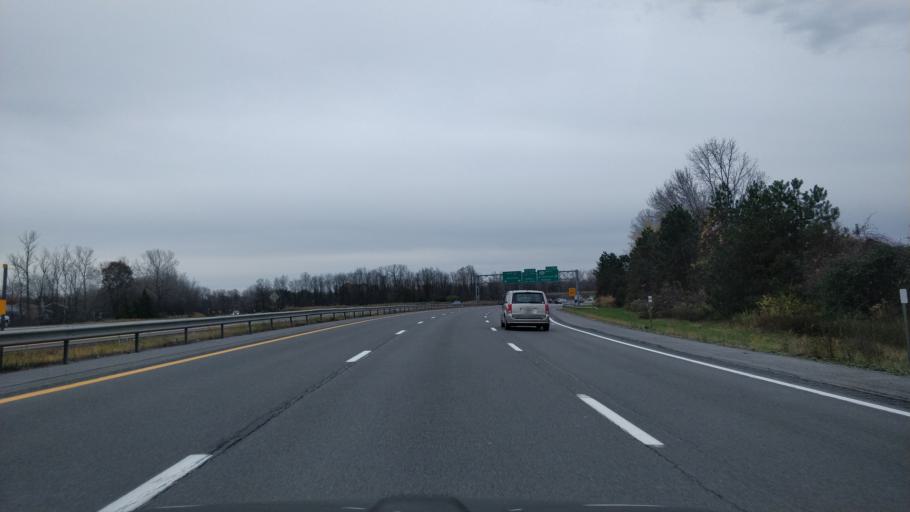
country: US
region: New York
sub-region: Onondaga County
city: North Syracuse
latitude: 43.1471
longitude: -76.1101
